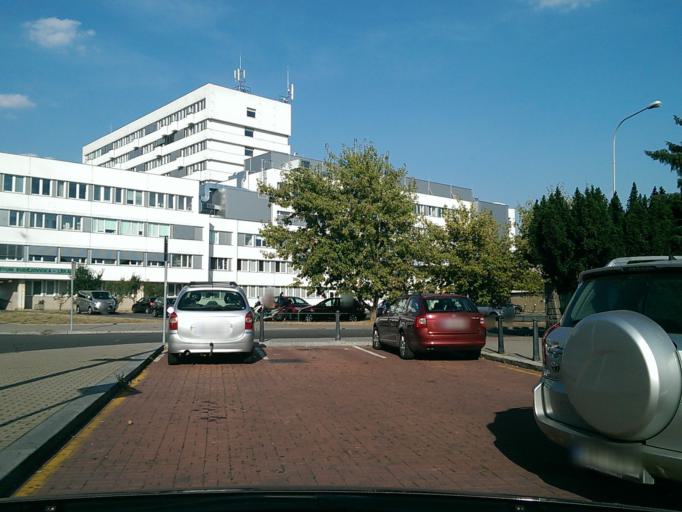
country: CZ
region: Praha
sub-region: Praha 4
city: Hodkovicky
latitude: 50.0425
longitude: 14.4487
